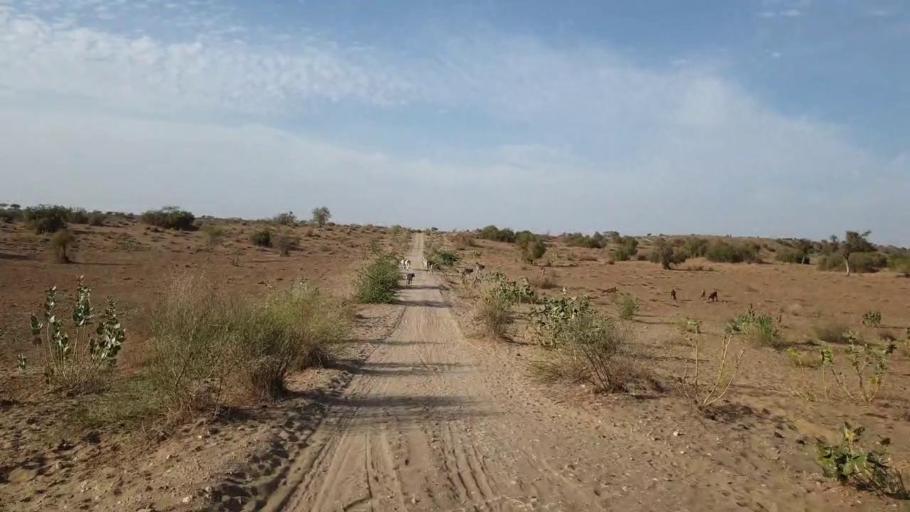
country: PK
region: Sindh
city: Nabisar
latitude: 25.0100
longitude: 69.9204
